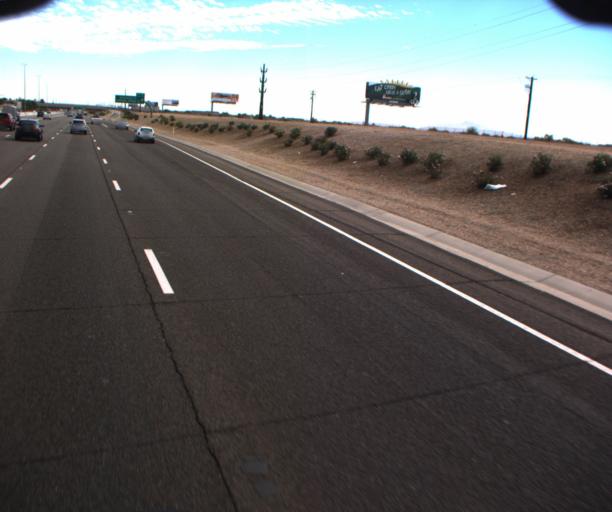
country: US
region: Arizona
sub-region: Maricopa County
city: Chandler
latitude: 33.2914
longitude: -111.9205
